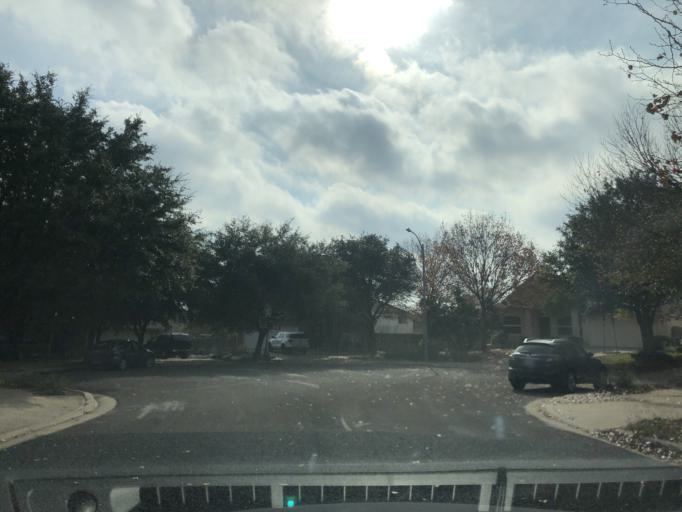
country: US
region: Texas
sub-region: Travis County
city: Wells Branch
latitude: 30.4264
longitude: -97.6800
